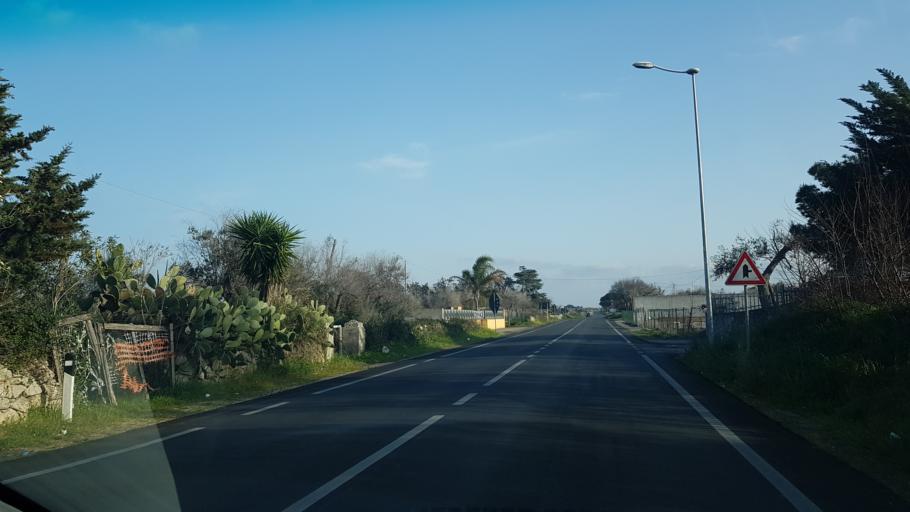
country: IT
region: Apulia
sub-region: Provincia di Lecce
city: Squinzano
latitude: 40.4267
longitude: 18.0538
